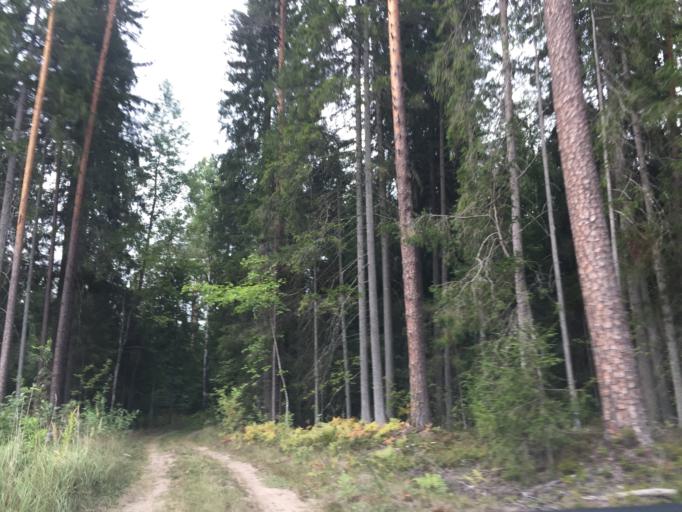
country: LV
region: Baldone
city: Baldone
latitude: 56.7758
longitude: 24.4448
